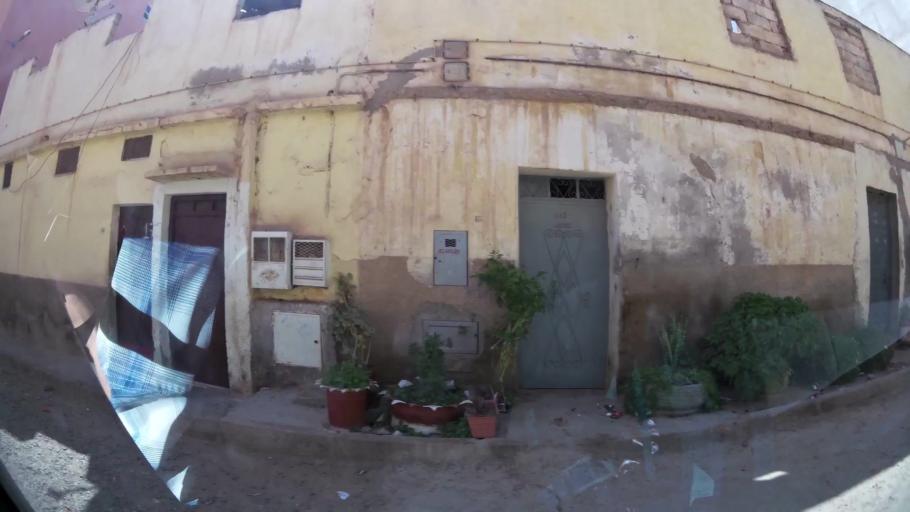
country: MA
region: Souss-Massa-Draa
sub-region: Inezgane-Ait Mellou
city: Inezgane
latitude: 30.3478
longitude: -9.5343
